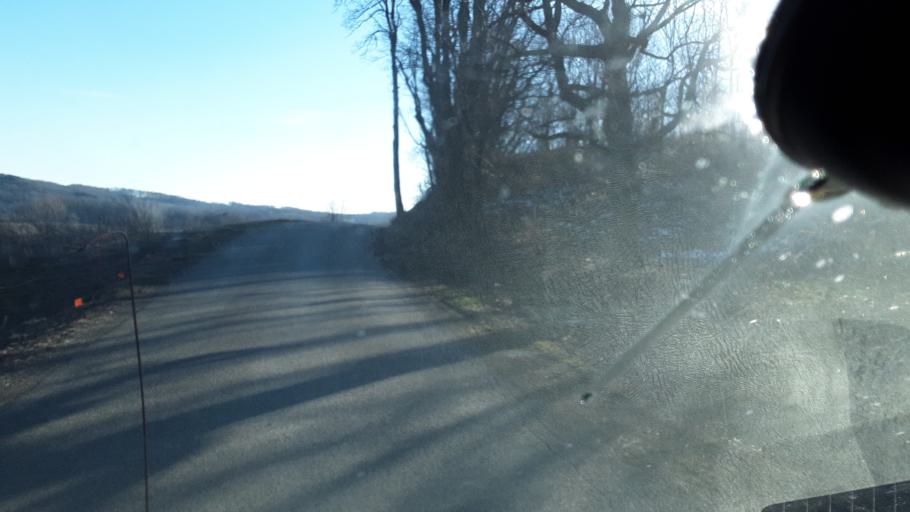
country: US
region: Ohio
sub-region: Ashland County
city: Loudonville
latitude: 40.6566
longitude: -82.2096
